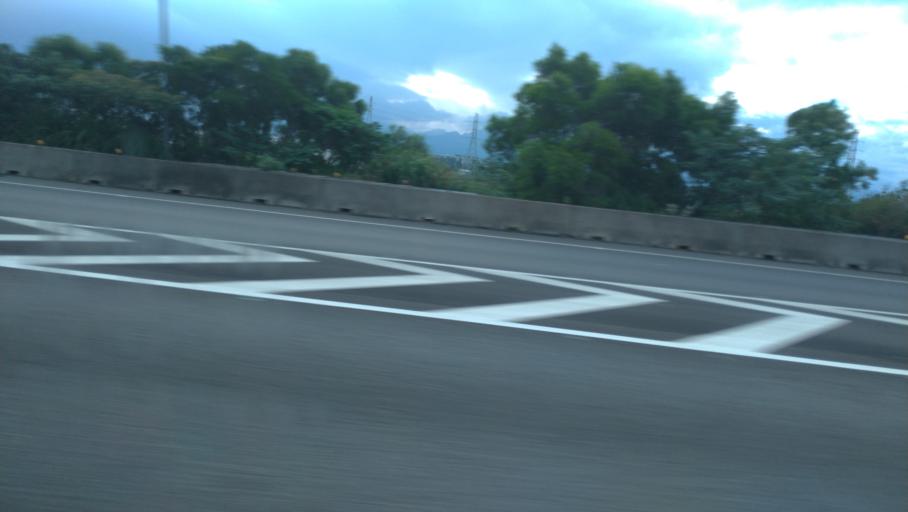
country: TW
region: Taiwan
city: Daxi
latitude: 24.8958
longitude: 121.2664
